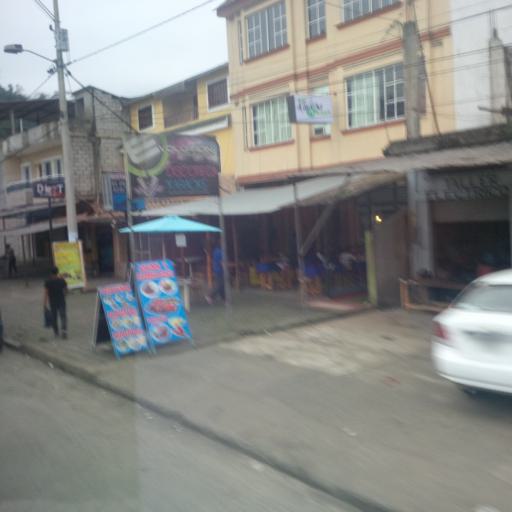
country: EC
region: Chimborazo
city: Alausi
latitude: -2.2040
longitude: -79.1321
